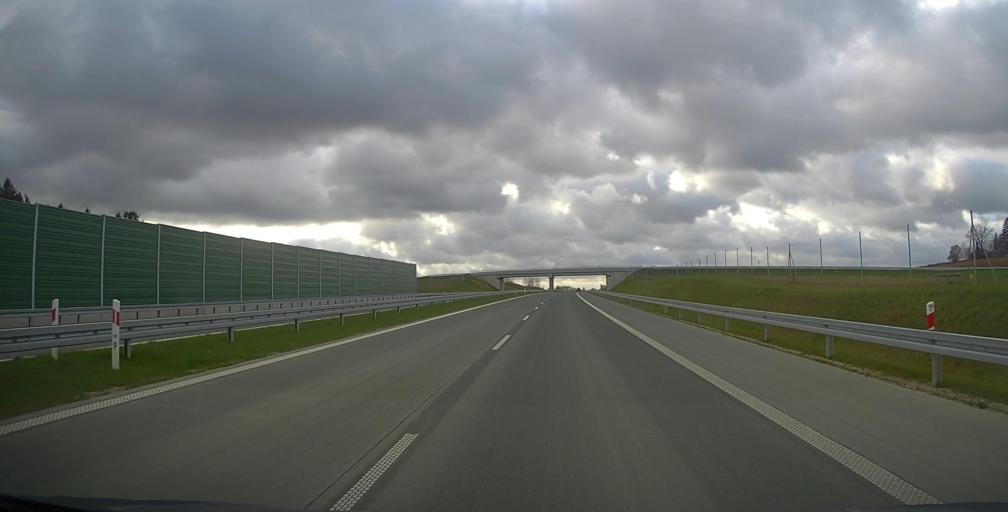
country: PL
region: Podlasie
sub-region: Powiat suwalski
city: Raczki
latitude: 53.9264
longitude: 22.7525
